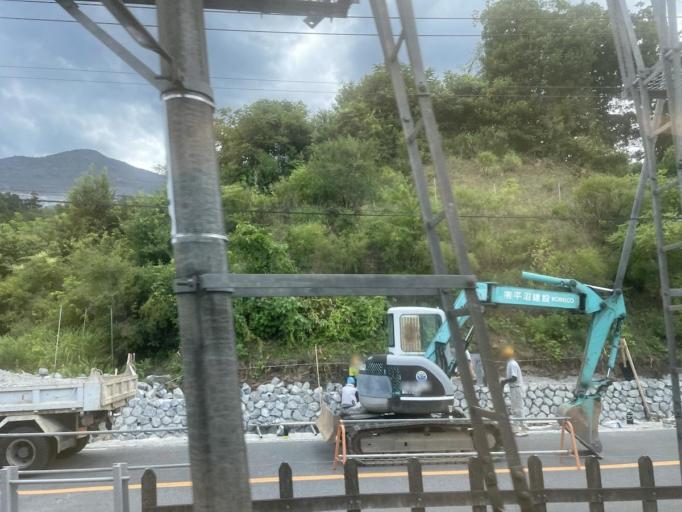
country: JP
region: Saitama
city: Chichibu
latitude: 35.9782
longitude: 139.1041
